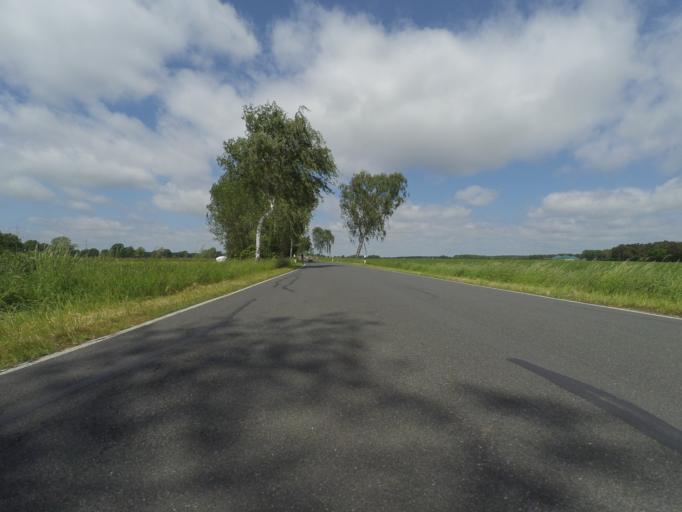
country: DE
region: Lower Saxony
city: Hillerse
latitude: 52.4024
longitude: 10.3410
